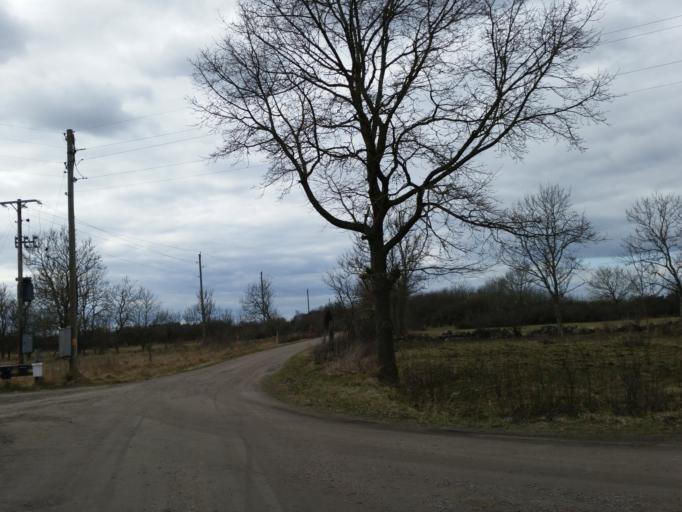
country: SE
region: Kalmar
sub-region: Morbylanga Kommun
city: Sodra Sandby
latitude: 56.6611
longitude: 16.6985
